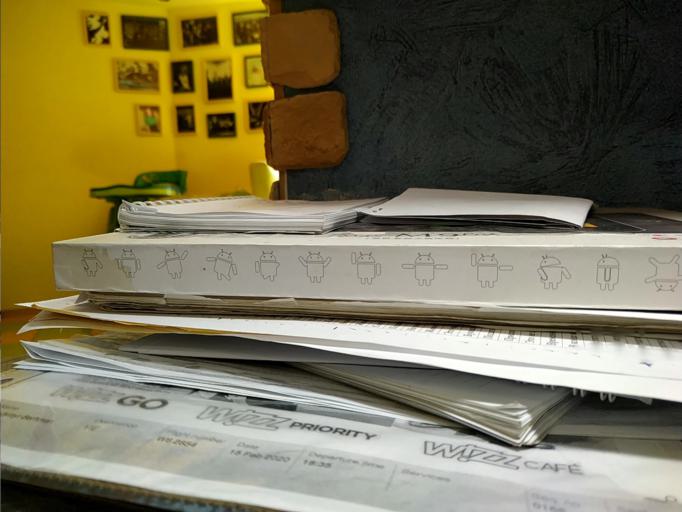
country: RU
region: Novgorod
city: Utorgosh
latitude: 58.1490
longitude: 30.0425
